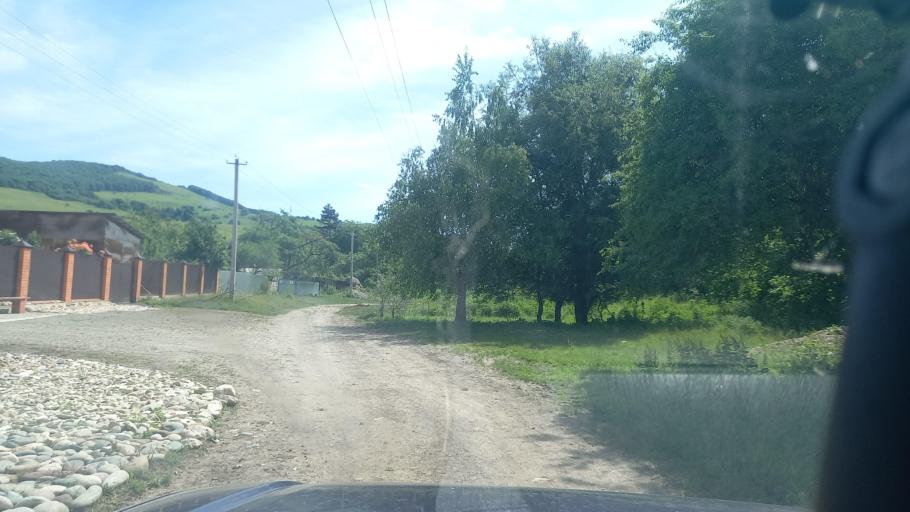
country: RU
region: Karachayevo-Cherkesiya
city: Kurdzhinovo
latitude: 44.1422
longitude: 41.0493
